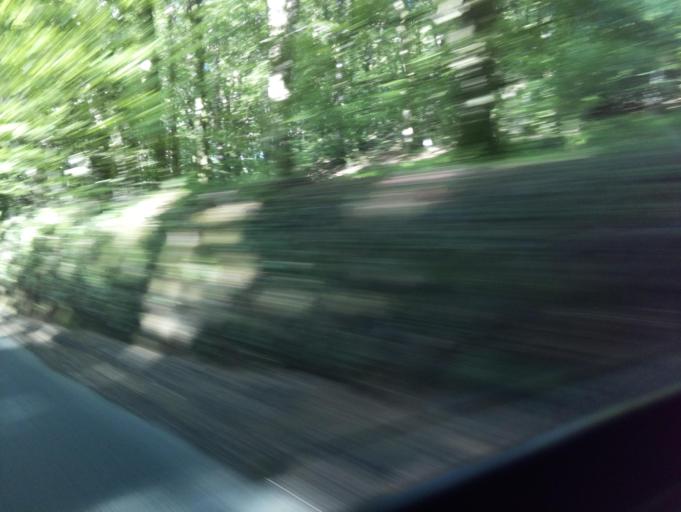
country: GB
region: England
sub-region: Dorset
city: Lyme Regis
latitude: 50.7890
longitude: -2.8946
